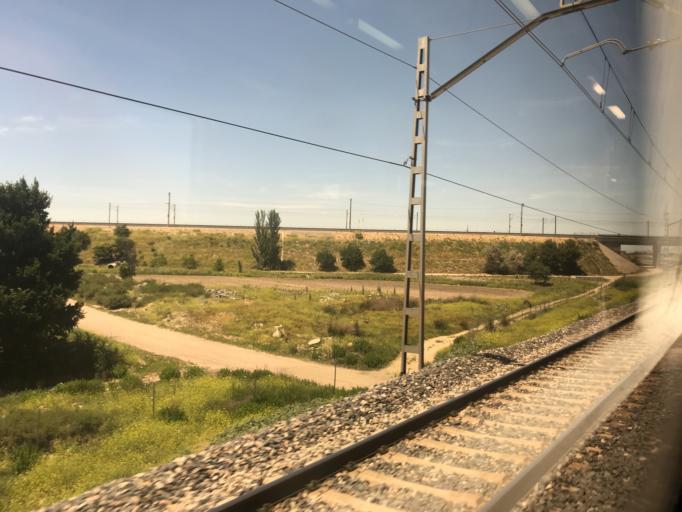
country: ES
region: Madrid
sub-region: Provincia de Madrid
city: Pinto
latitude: 40.2791
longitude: -3.7040
